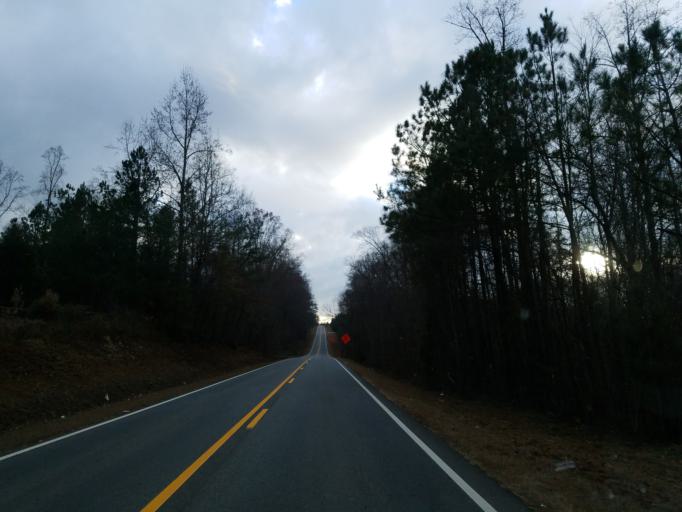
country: US
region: Georgia
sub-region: Dawson County
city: Dawsonville
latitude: 34.3303
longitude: -84.0691
